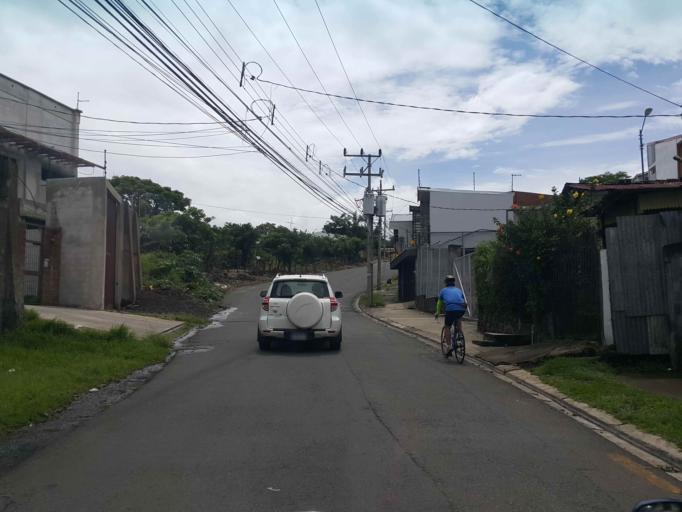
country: CR
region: Heredia
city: Heredia
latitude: 10.0159
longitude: -84.1159
